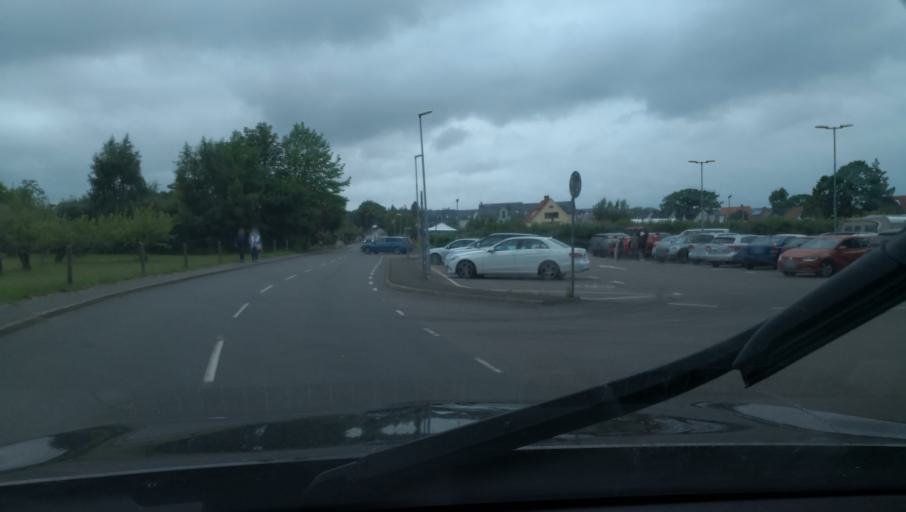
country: SE
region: Skane
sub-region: Simrishamns Kommun
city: Kivik
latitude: 55.6831
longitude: 14.2336
